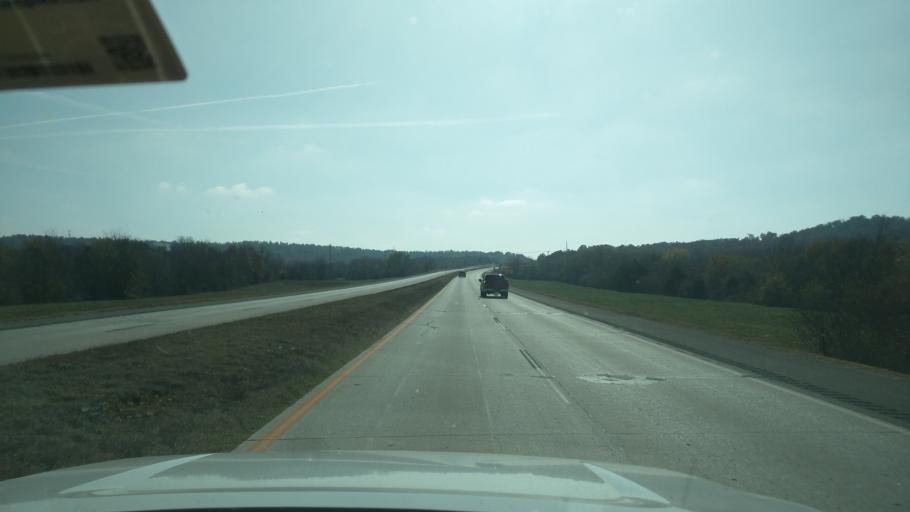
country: US
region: Oklahoma
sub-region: Muskogee County
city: Muskogee
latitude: 35.6711
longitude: -95.3090
